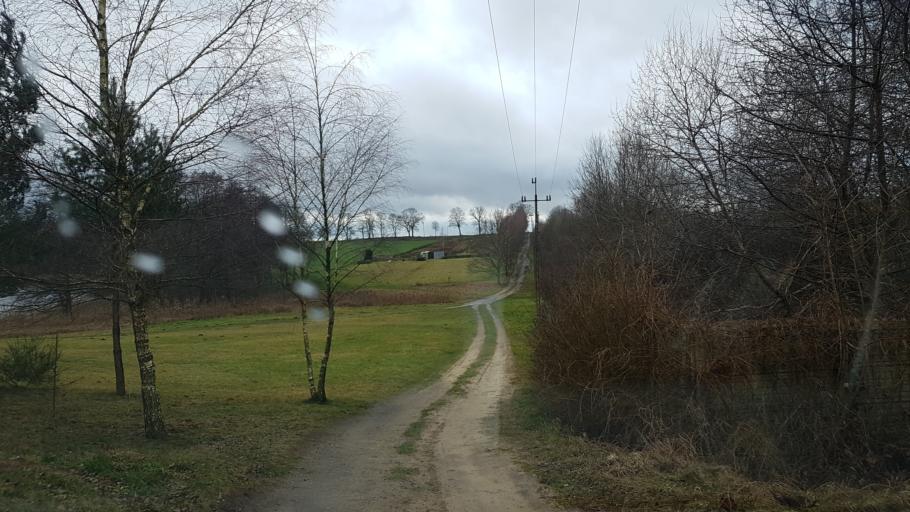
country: PL
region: West Pomeranian Voivodeship
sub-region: Powiat drawski
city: Czaplinek
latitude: 53.5498
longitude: 16.2491
